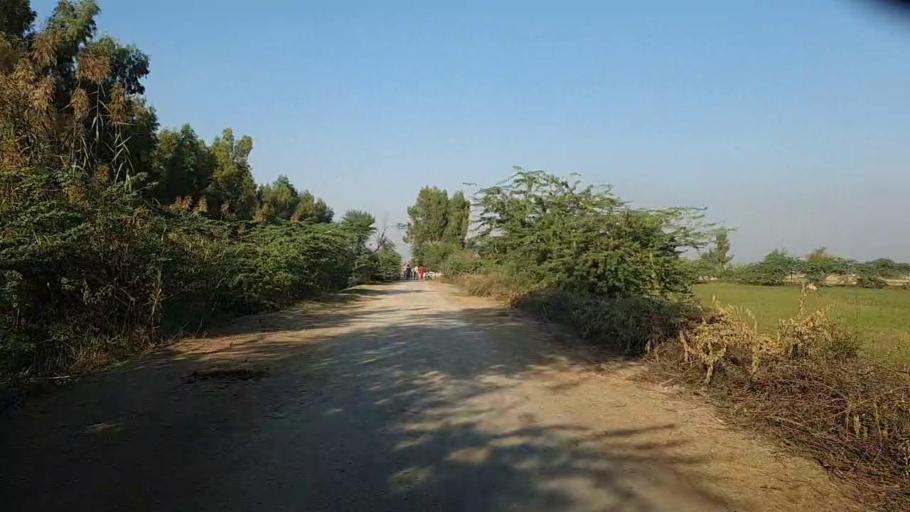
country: PK
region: Sindh
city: Ranipur
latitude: 27.2490
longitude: 68.5062
